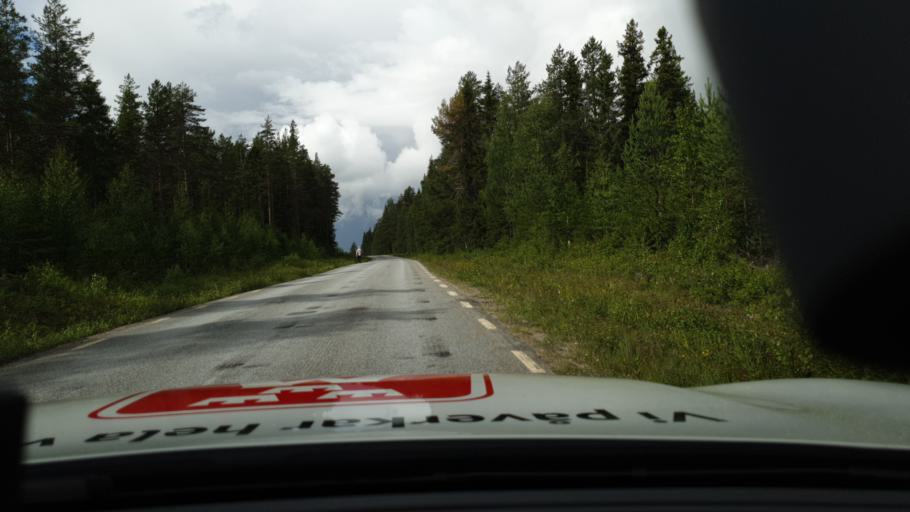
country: SE
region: Norrbotten
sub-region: Pitea Kommun
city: Rosvik
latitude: 65.4175
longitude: 21.7837
